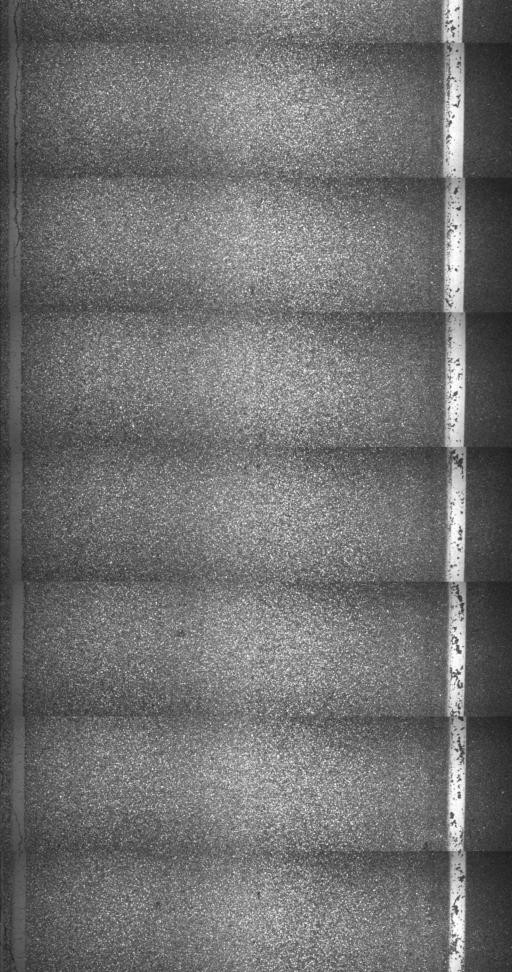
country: US
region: Vermont
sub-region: Rutland County
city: Rutland
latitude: 43.5405
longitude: -72.7481
